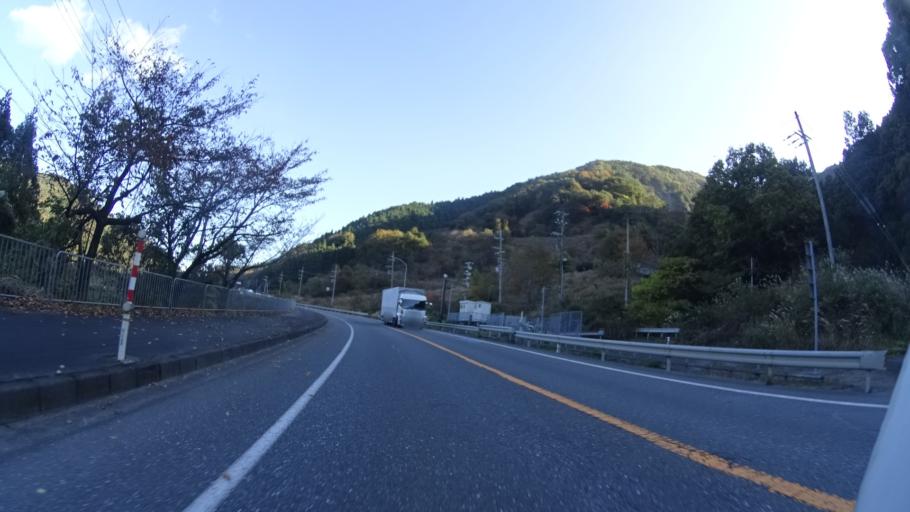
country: JP
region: Fukui
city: Tsuruga
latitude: 35.4722
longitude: 136.0802
